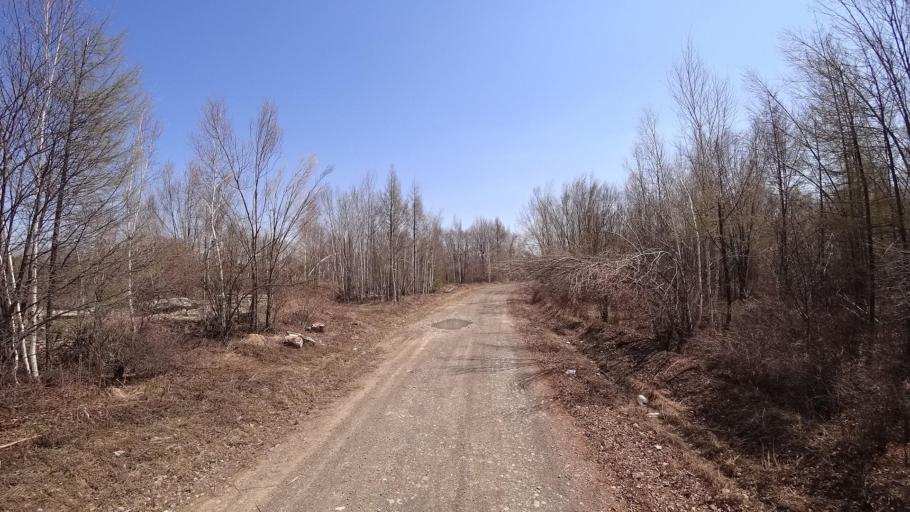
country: RU
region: Khabarovsk Krai
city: Khurba
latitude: 50.4086
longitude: 136.8484
